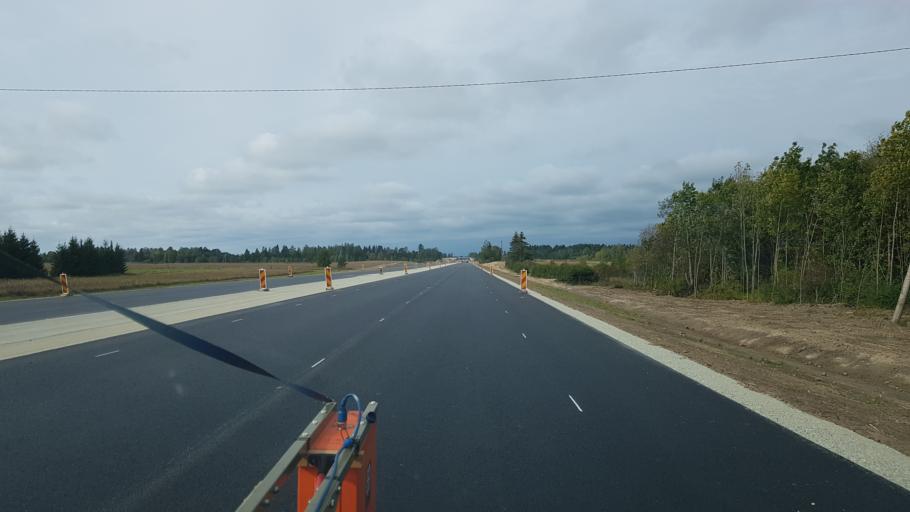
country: EE
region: Laeaene-Virumaa
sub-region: Haljala vald
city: Haljala
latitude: 59.4351
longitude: 26.1698
